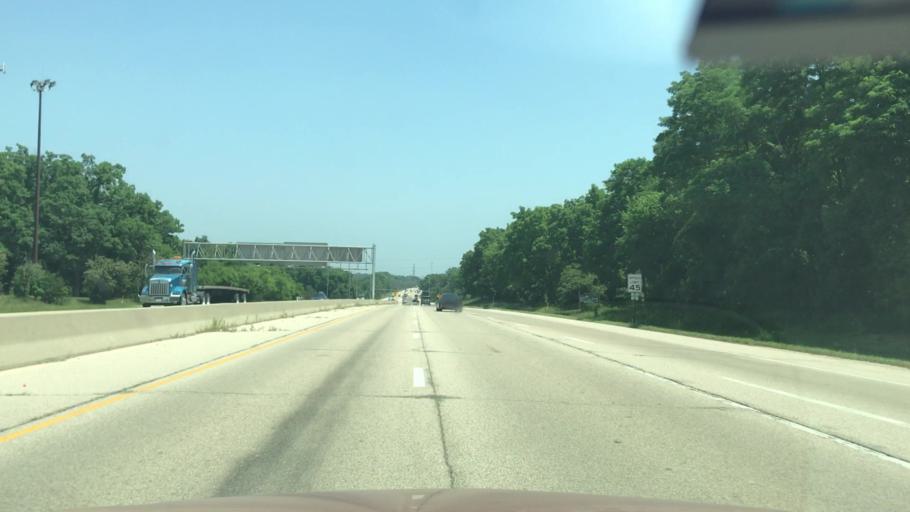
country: US
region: Illinois
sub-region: Winnebago County
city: Cherry Valley
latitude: 42.2389
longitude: -88.9615
